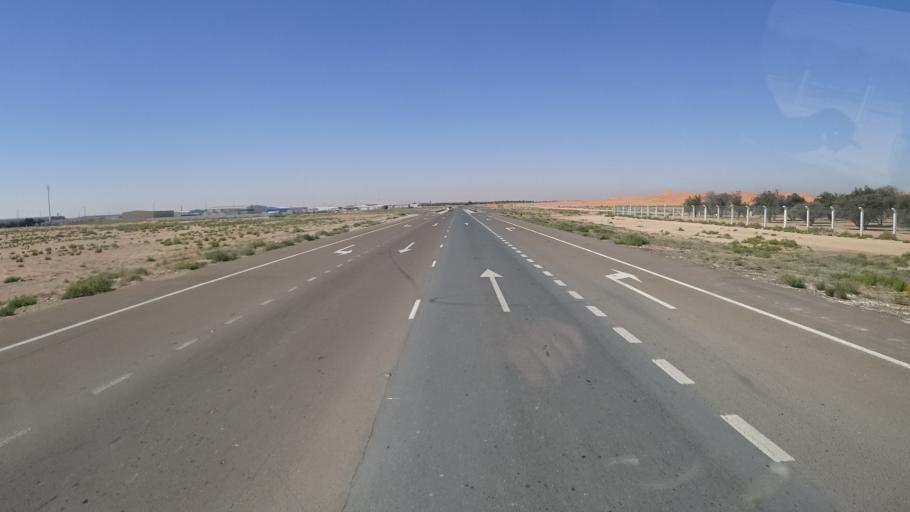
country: AE
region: Abu Dhabi
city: Al Ain
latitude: 24.0811
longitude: 55.6560
